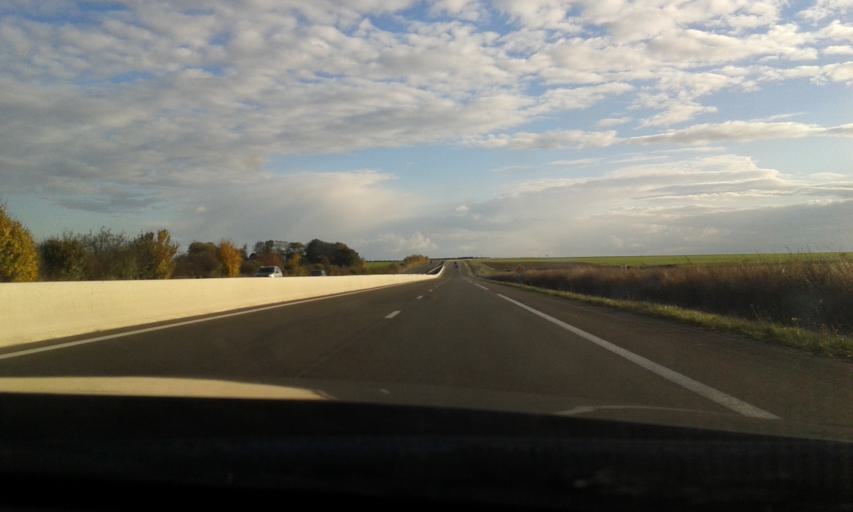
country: FR
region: Centre
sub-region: Departement d'Eure-et-Loir
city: Bailleau-l'Eveque
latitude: 48.5587
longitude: 1.4430
